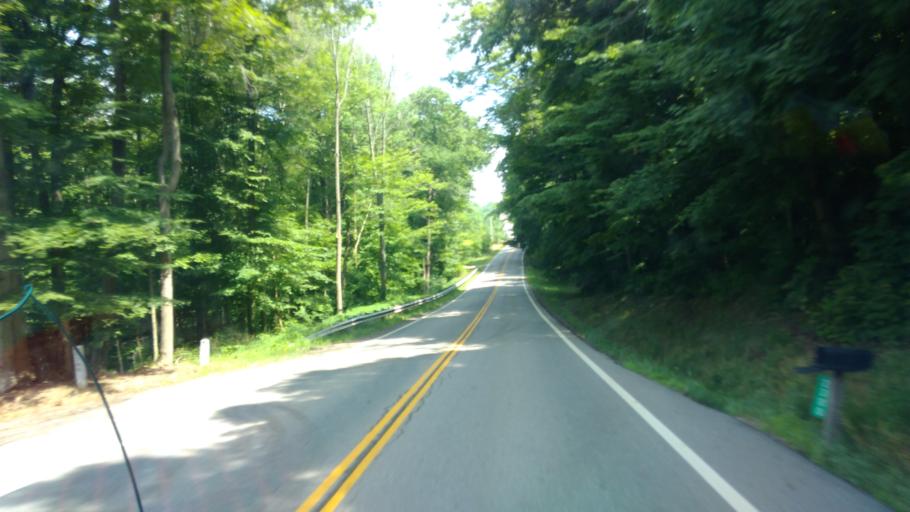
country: US
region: Ohio
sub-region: Ashland County
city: Loudonville
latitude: 40.7248
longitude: -82.3178
